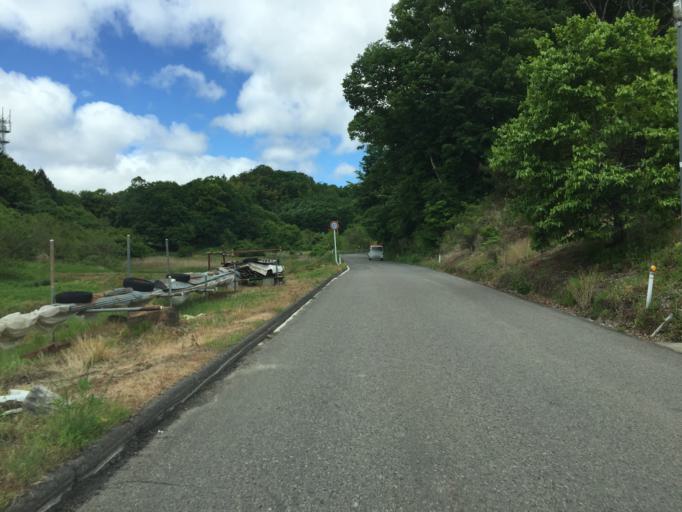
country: JP
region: Fukushima
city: Miharu
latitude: 37.4636
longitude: 140.4686
